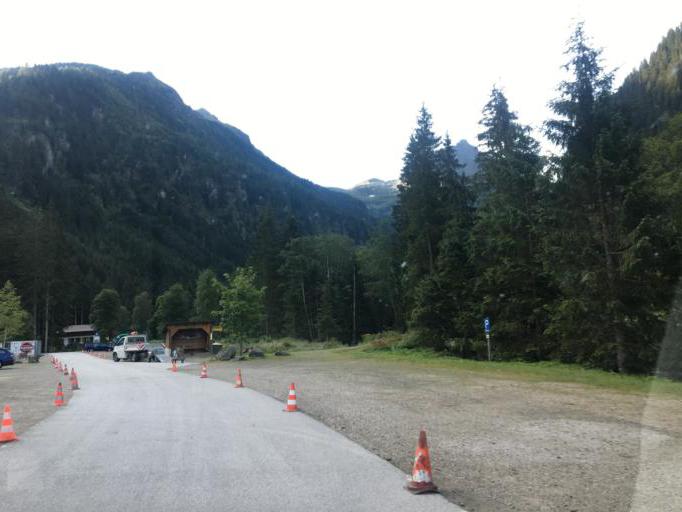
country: AT
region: Styria
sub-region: Politischer Bezirk Liezen
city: Haus
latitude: 47.3277
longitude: 13.7582
